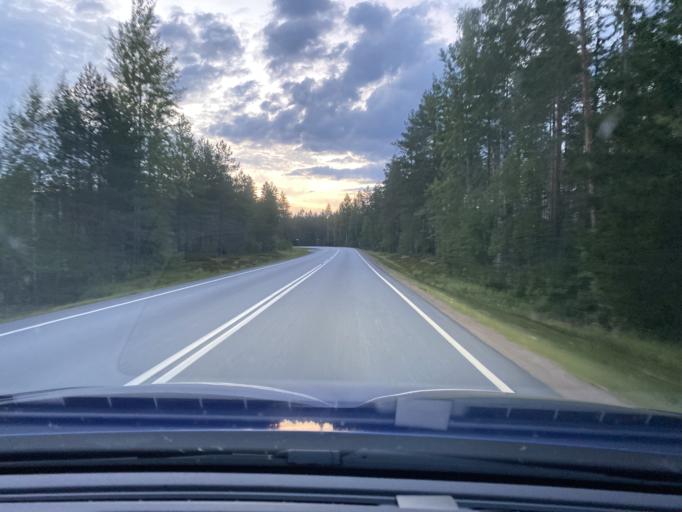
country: FI
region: Southern Ostrobothnia
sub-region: Suupohja
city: Kauhajoki
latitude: 62.2529
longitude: 22.2701
